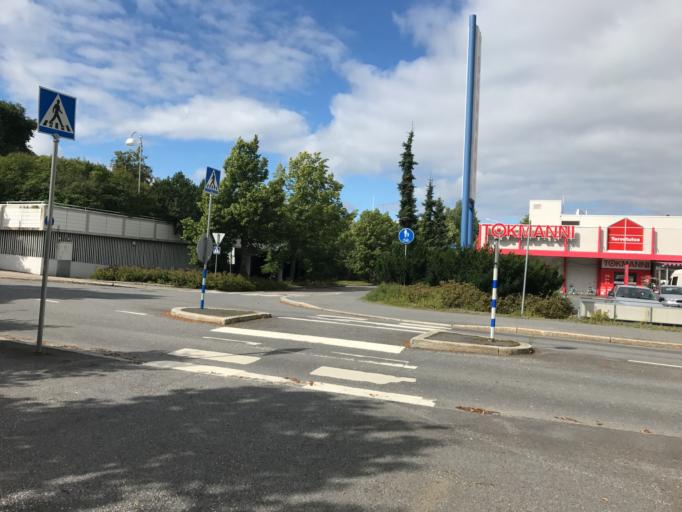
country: FI
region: Pirkanmaa
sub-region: Etelae-Pirkanmaa
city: Valkeakoski
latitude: 61.2636
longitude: 24.0360
